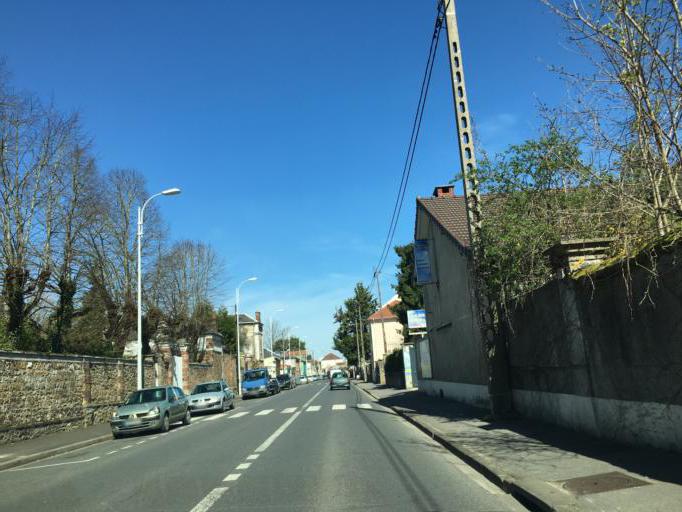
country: FR
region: Ile-de-France
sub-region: Departement de l'Essonne
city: Draveil
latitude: 48.6770
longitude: 2.4109
